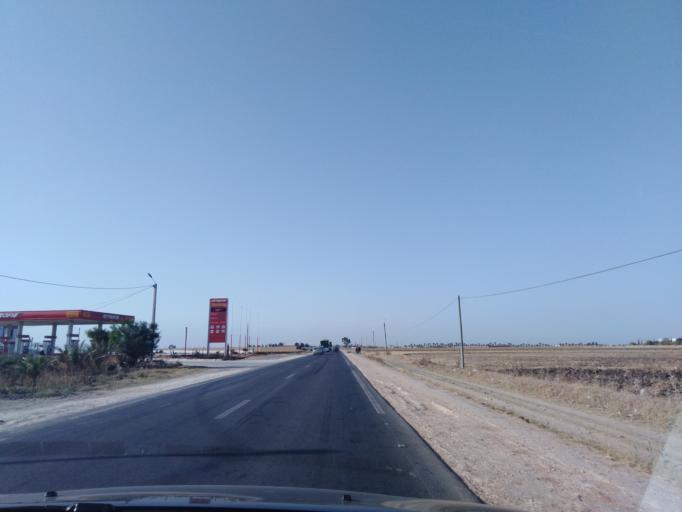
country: MA
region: Doukkala-Abda
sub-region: El-Jadida
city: Sidi Bennour
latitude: 32.5951
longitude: -8.7076
